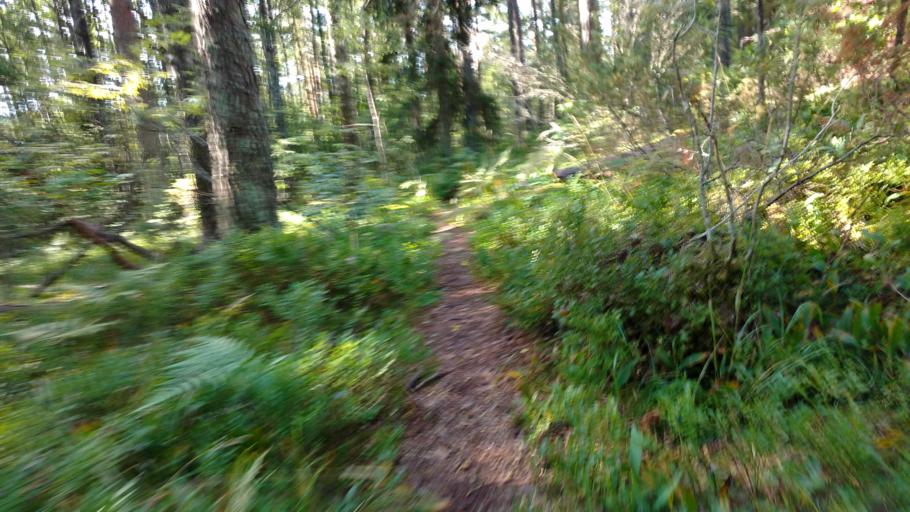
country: FI
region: Varsinais-Suomi
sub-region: Salo
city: Salo
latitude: 60.3801
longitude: 23.1711
